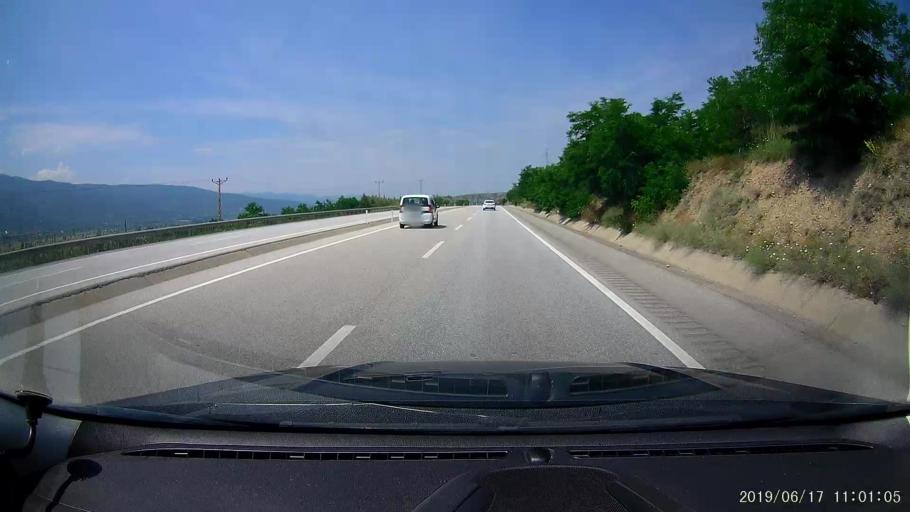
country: TR
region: Kastamonu
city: Tosya
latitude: 41.0296
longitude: 34.1640
